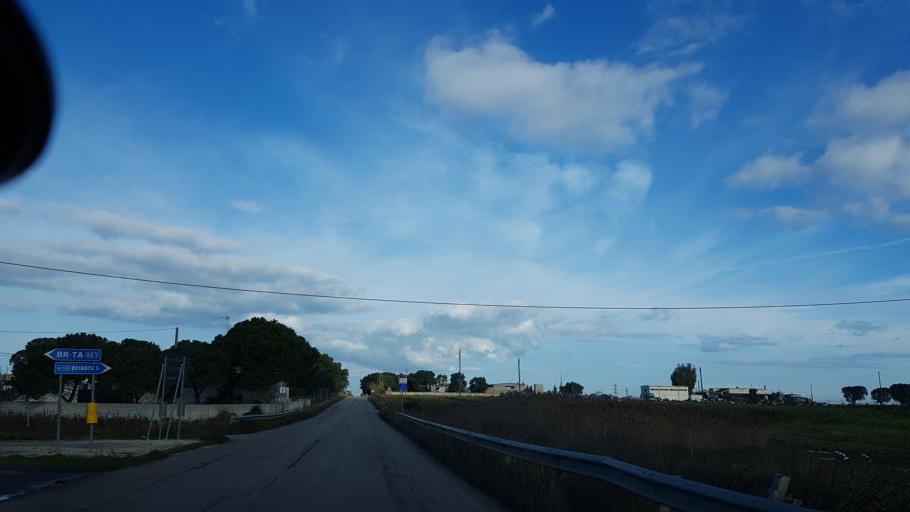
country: IT
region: Apulia
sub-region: Provincia di Brindisi
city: La Rosa
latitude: 40.5941
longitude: 17.9594
